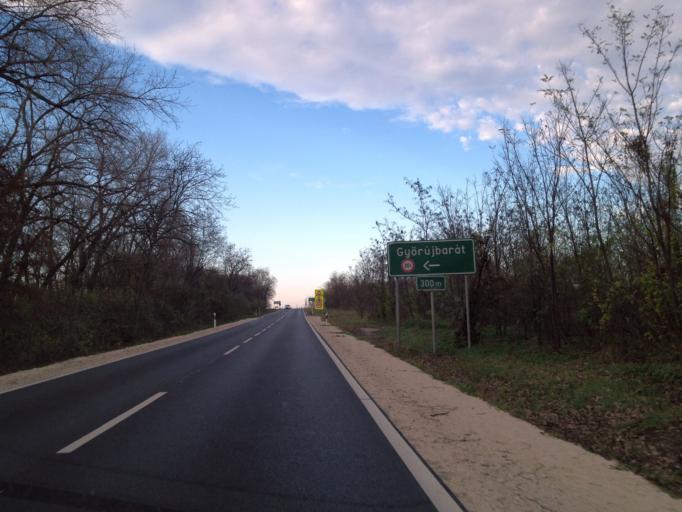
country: HU
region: Gyor-Moson-Sopron
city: Nyul
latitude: 47.6190
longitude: 17.6782
